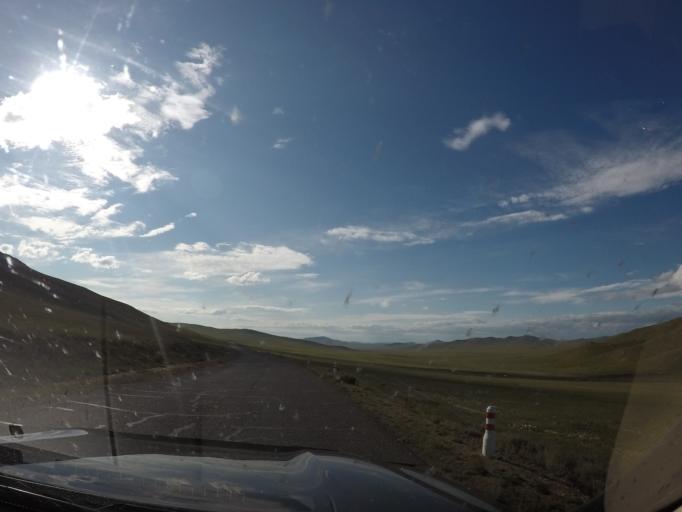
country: MN
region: Hentiy
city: Modot
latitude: 47.8087
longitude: 108.8047
